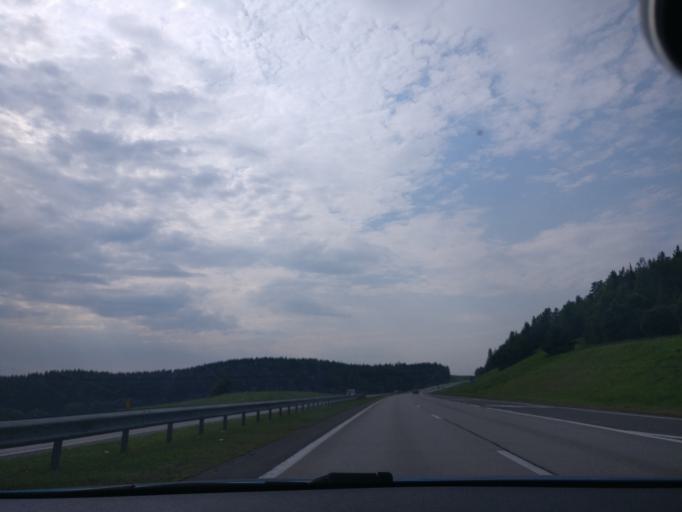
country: BY
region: Minsk
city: Lahoysk
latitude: 54.1117
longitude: 27.8039
